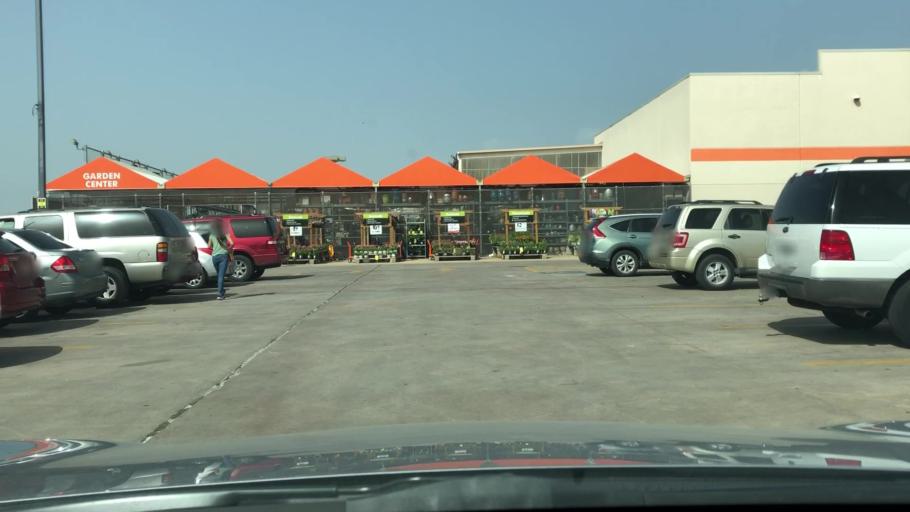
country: US
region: Texas
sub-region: Bexar County
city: Live Oak
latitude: 29.5661
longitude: -98.3286
